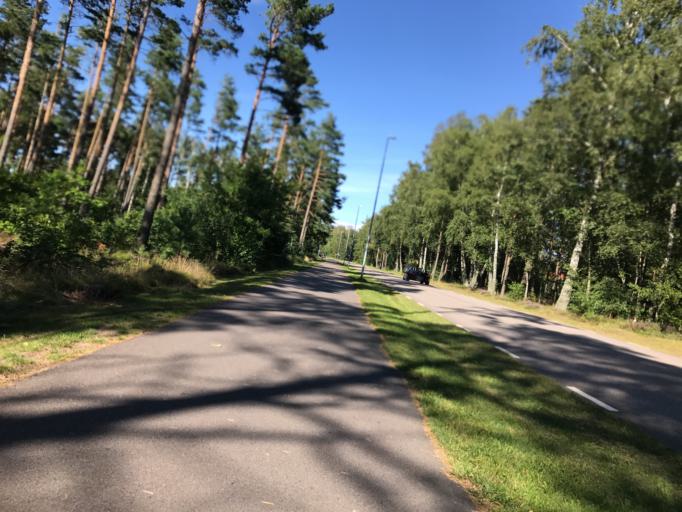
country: SE
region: Skane
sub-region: Bastads Kommun
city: Bastad
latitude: 56.4449
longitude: 12.9011
